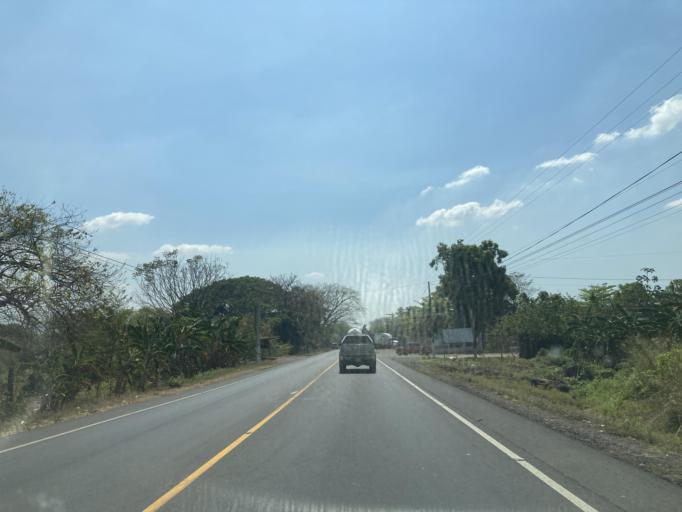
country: GT
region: Escuintla
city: Guanagazapa
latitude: 14.2258
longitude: -90.7333
